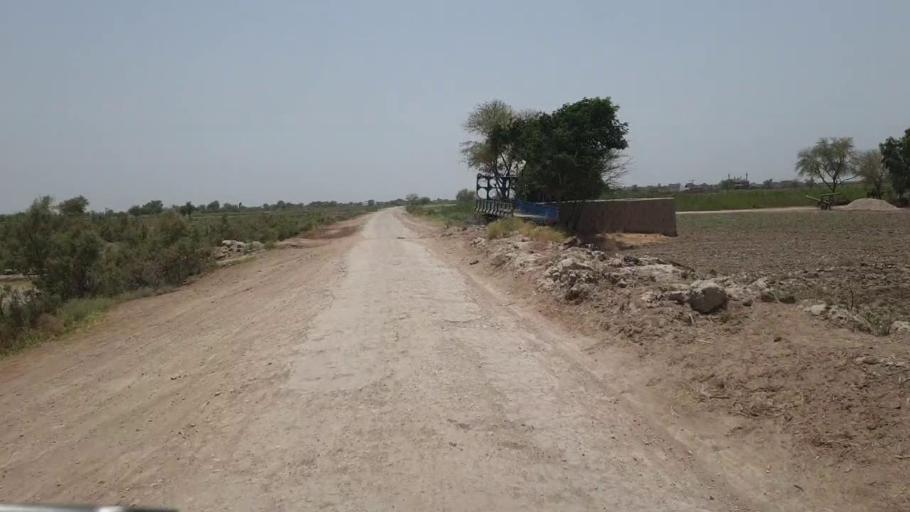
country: PK
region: Sindh
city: Daulatpur
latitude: 26.4621
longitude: 68.1314
